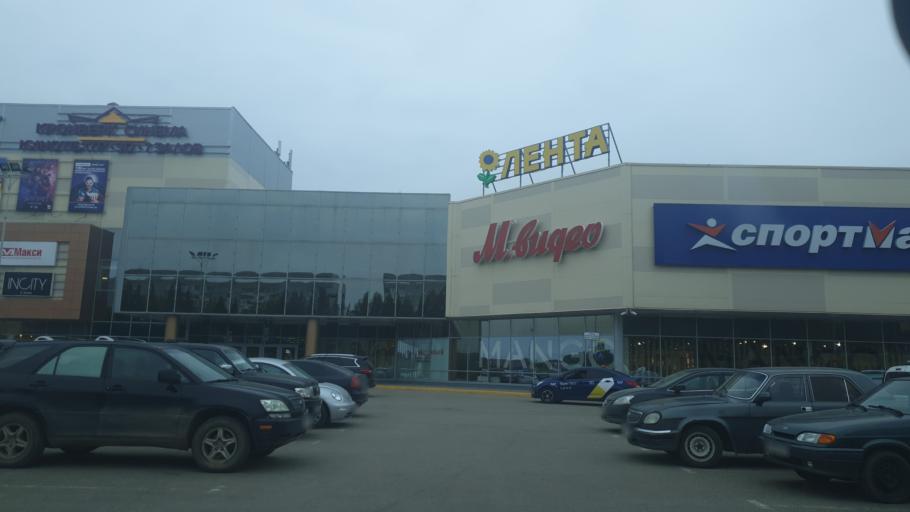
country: RU
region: Komi Republic
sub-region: Syktyvdinskiy Rayon
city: Syktyvkar
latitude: 61.6981
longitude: 50.8039
